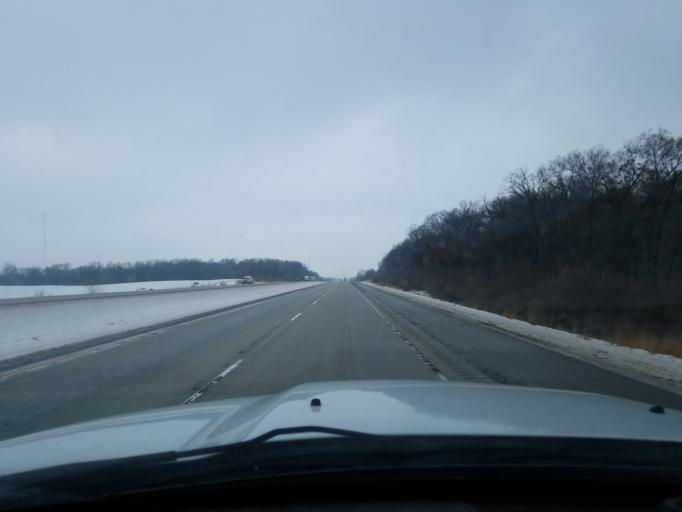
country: US
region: Indiana
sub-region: Fulton County
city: Rochester
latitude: 41.1260
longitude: -86.2397
